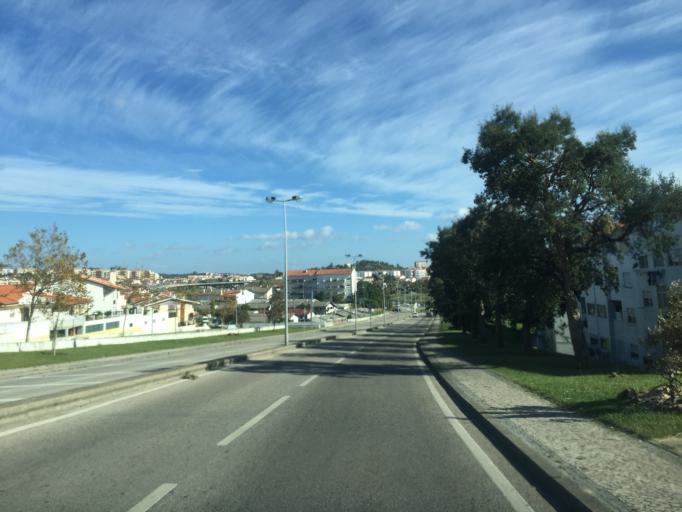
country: PT
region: Coimbra
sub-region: Figueira da Foz
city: Tavarede
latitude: 40.1644
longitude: -8.8509
